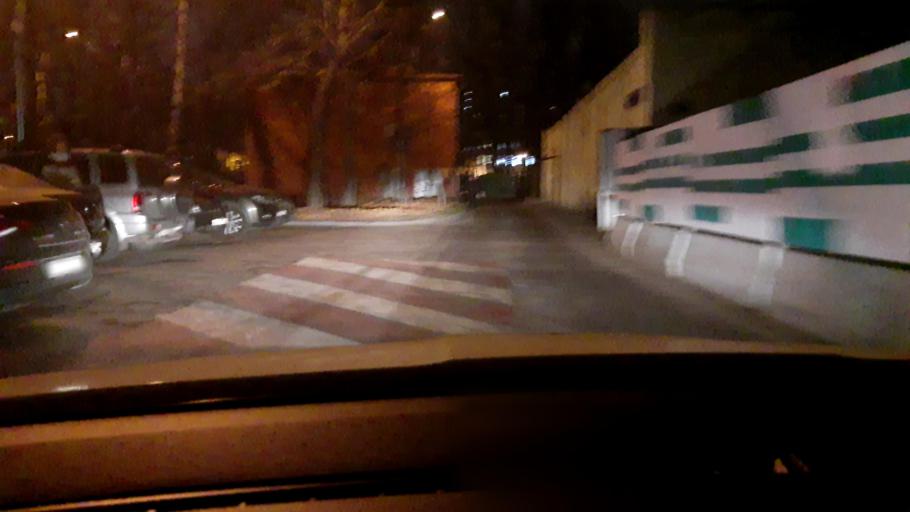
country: RU
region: Moscow
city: Metrogorodok
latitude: 55.8068
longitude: 37.7917
